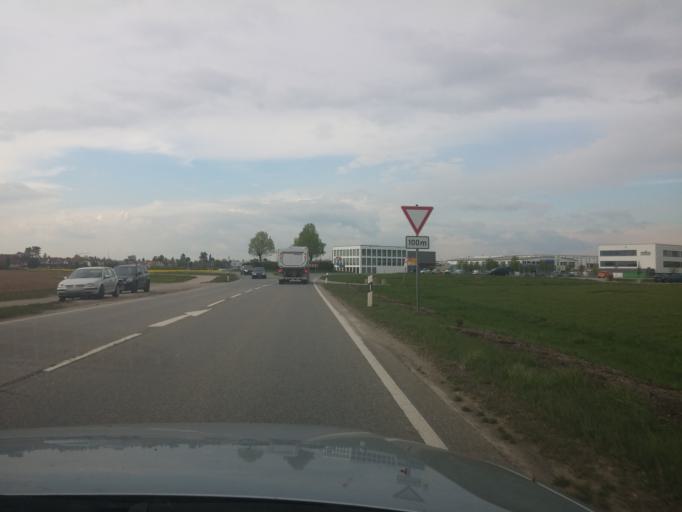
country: DE
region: Bavaria
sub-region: Upper Bavaria
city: Feldkirchen
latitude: 48.1377
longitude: 11.7361
